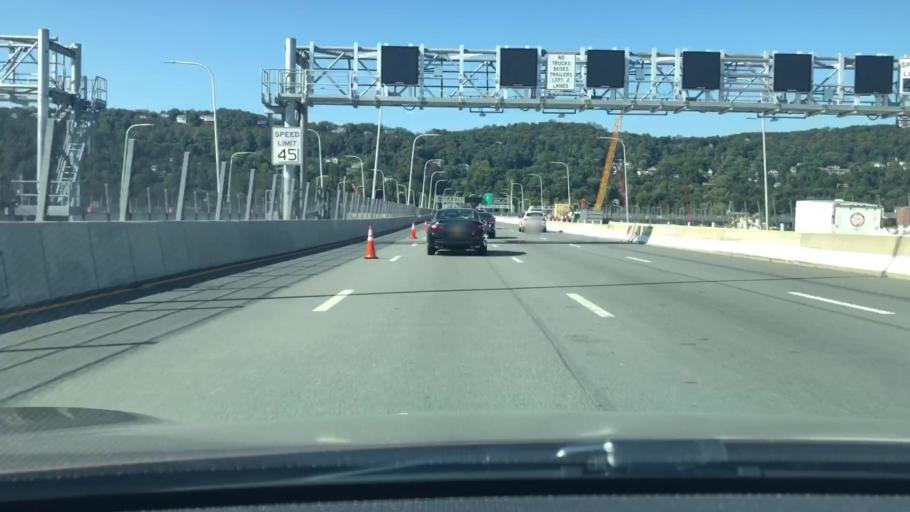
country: US
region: New York
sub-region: Rockland County
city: South Nyack
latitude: 41.0712
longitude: -73.9075
